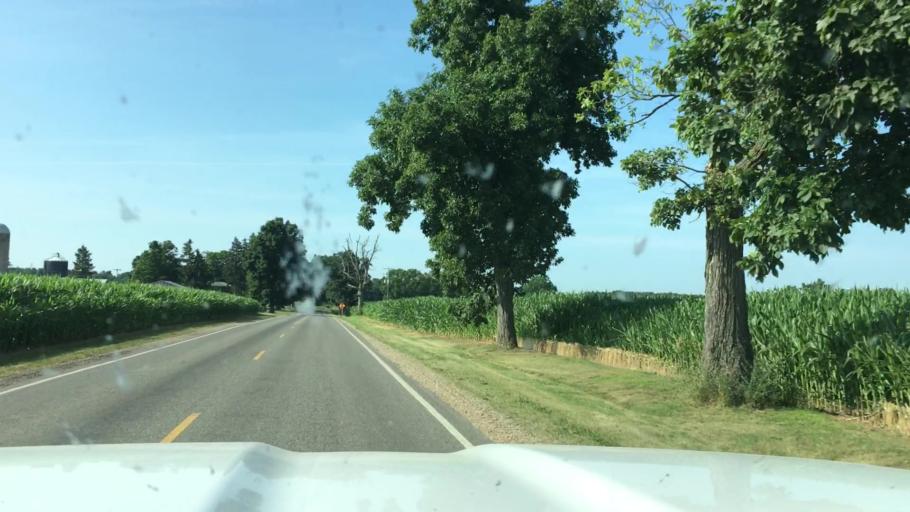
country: US
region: Michigan
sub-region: Barry County
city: Stony Point
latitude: 42.4600
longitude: -85.4447
